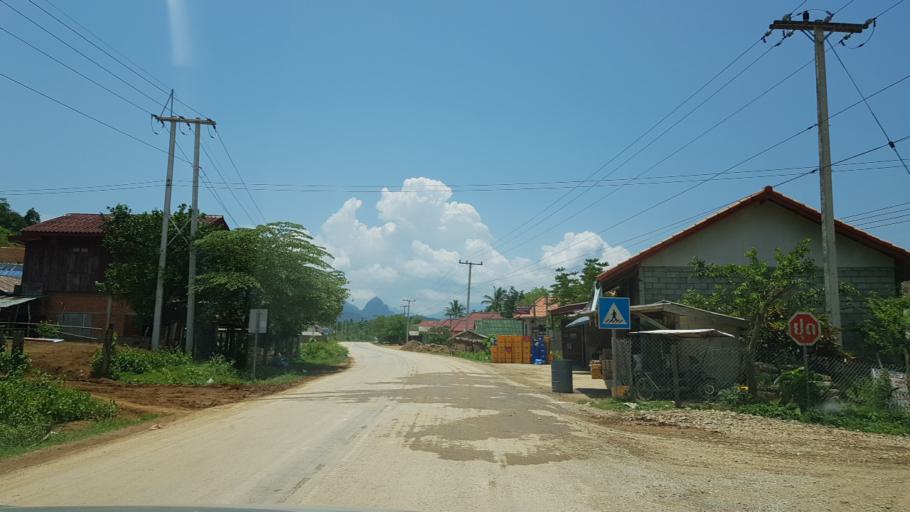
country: LA
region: Vientiane
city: Muang Kasi
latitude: 19.2679
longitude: 102.2289
